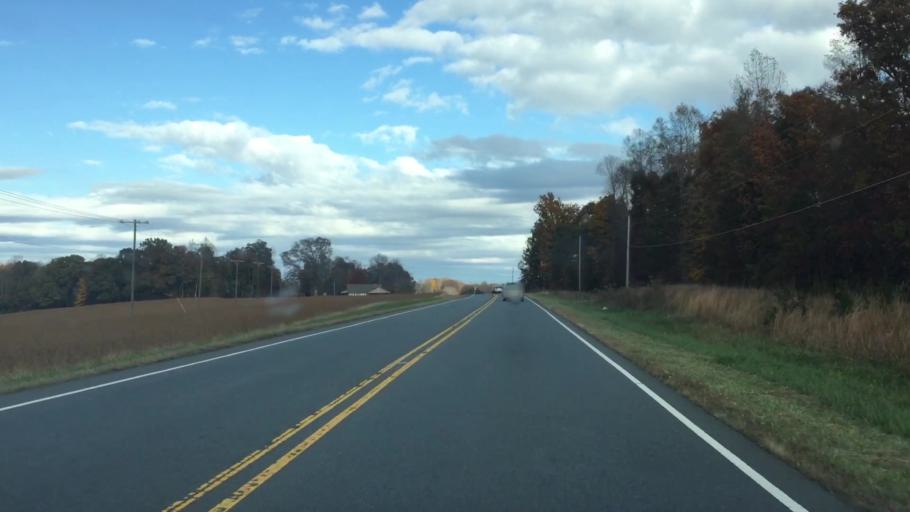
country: US
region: North Carolina
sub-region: Forsyth County
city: Walkertown
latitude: 36.1942
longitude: -80.0939
